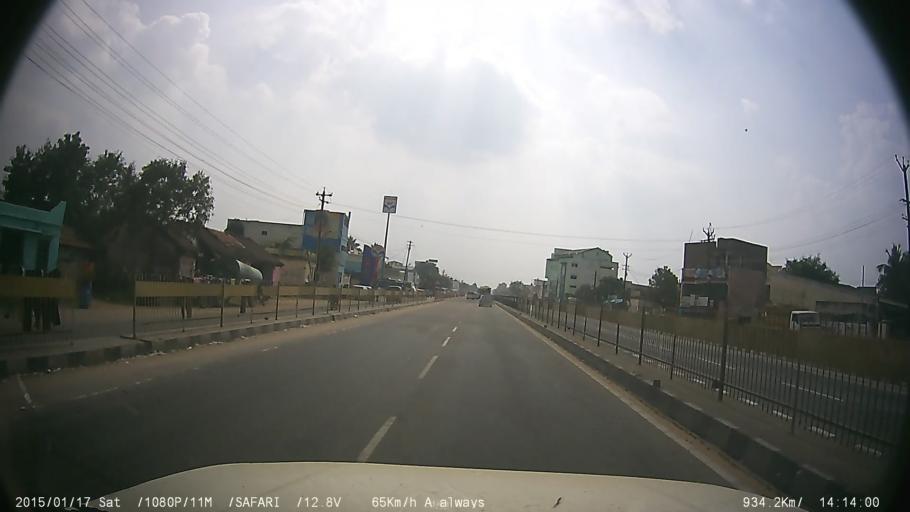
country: IN
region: Tamil Nadu
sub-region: Vellore
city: Ambur
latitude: 12.7789
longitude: 78.7167
